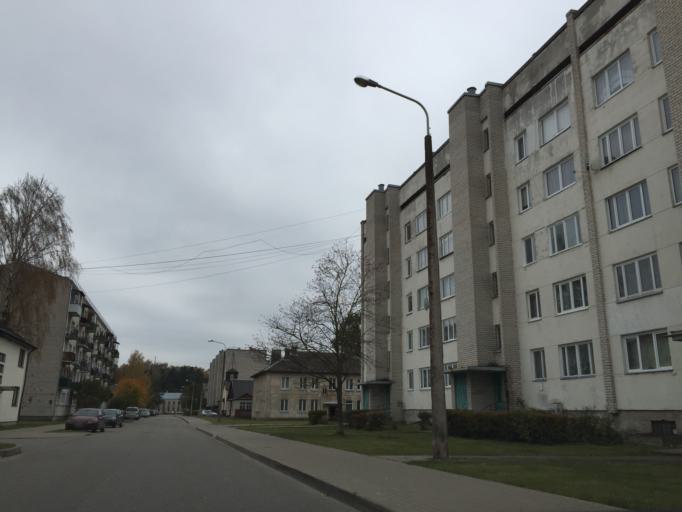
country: LV
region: Olaine
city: Olaine
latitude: 56.7882
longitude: 23.9371
